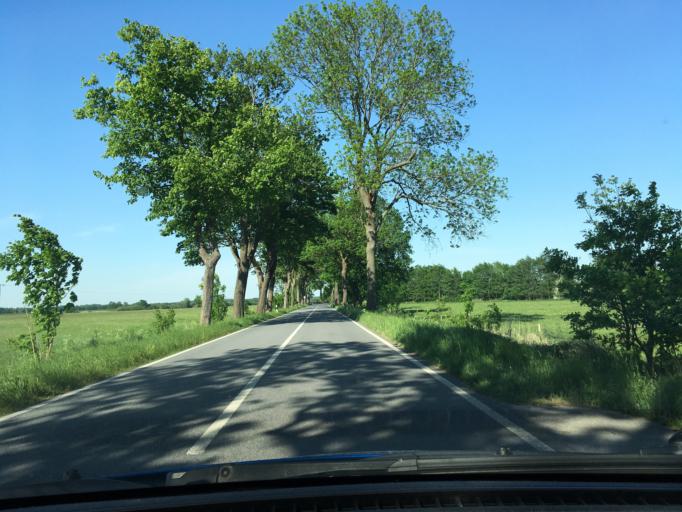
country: DE
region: Brandenburg
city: Lenzen
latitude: 53.0819
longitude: 11.4168
